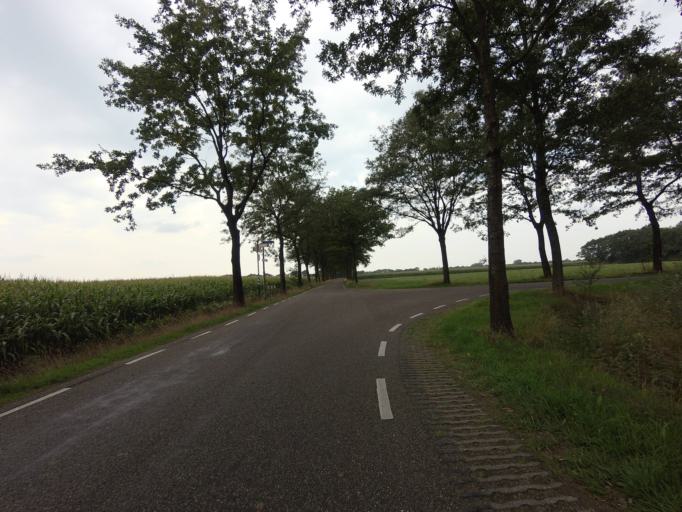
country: NL
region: Drenthe
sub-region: Gemeente Tynaarlo
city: Vries
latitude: 53.0467
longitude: 6.5891
